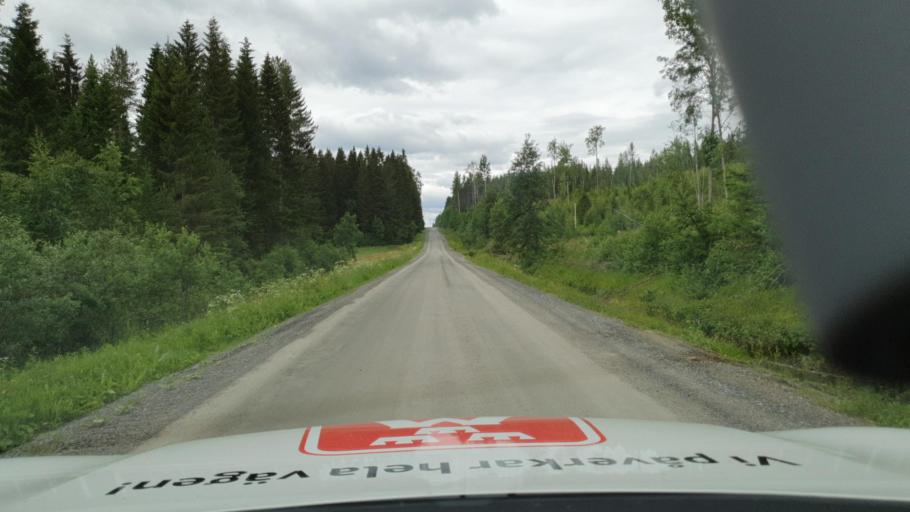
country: SE
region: Vaesterbotten
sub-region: Nordmalings Kommun
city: Nordmaling
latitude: 63.6897
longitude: 19.4442
